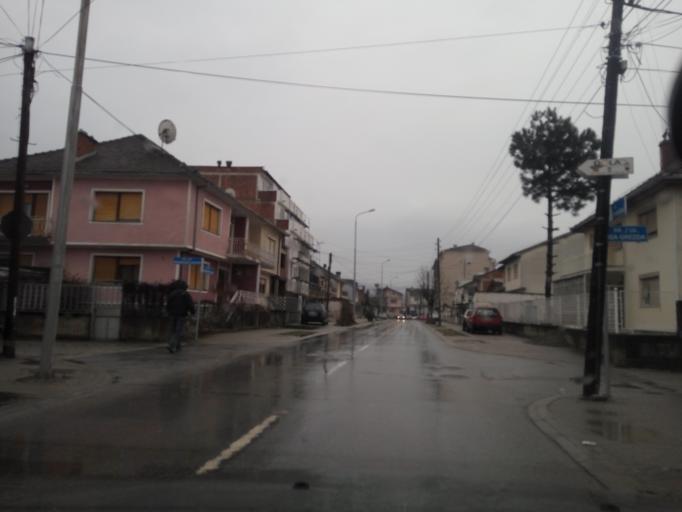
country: XK
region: Gjakova
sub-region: Komuna e Gjakoves
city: Gjakove
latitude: 42.3725
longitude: 20.4405
